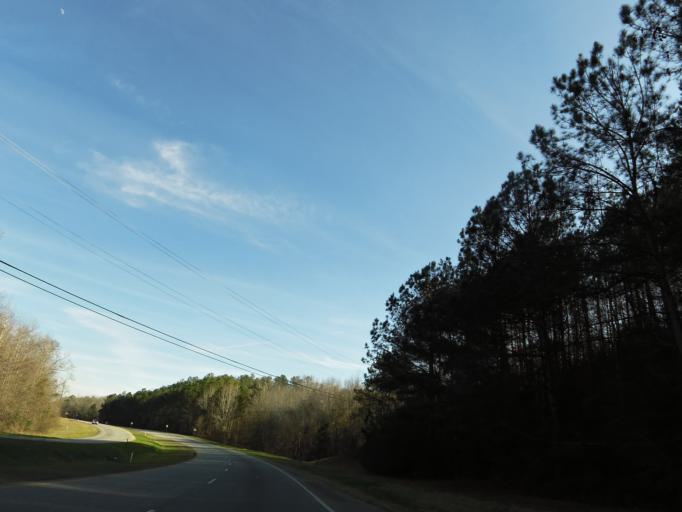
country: US
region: Georgia
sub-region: Chattahoochee County
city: Cusseta
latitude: 32.2652
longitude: -84.7411
